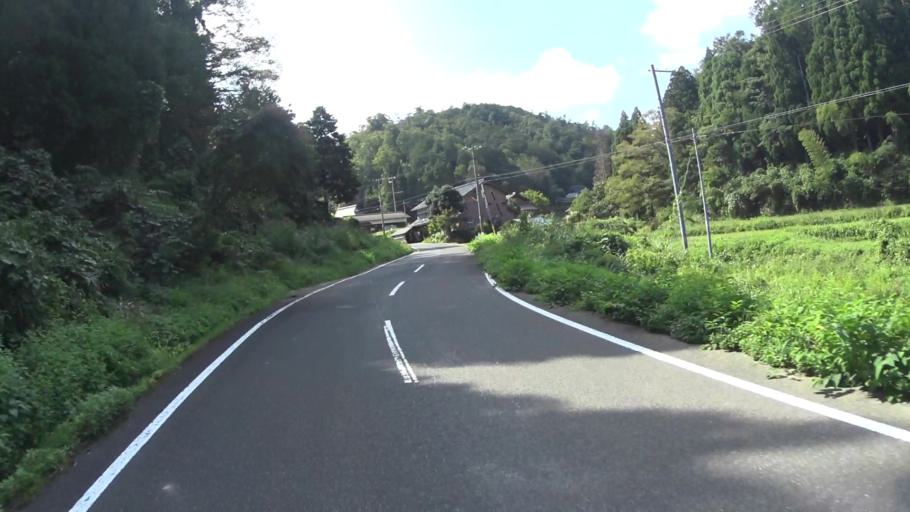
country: JP
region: Kyoto
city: Miyazu
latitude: 35.6748
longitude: 135.1497
